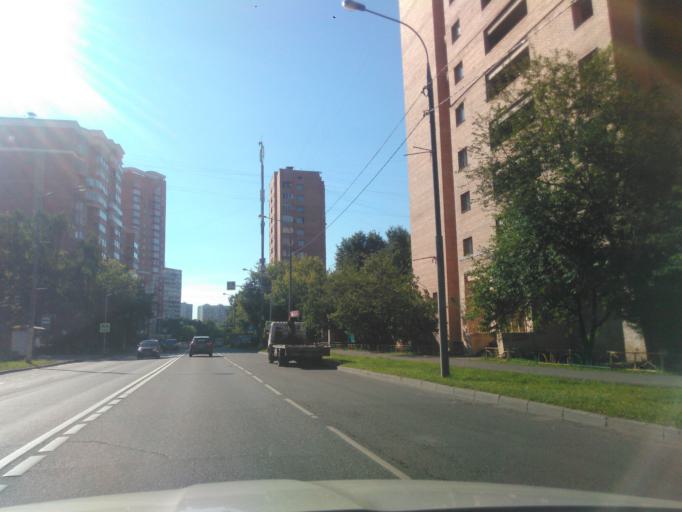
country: RU
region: Moscow
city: Novokhovrino
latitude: 55.8648
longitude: 37.4996
